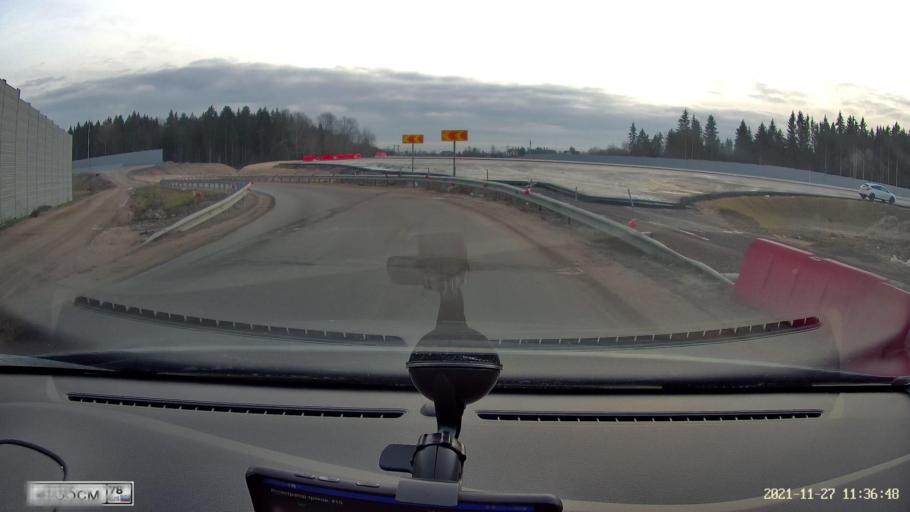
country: RU
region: Leningrad
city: Russko-Vysotskoye
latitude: 59.6971
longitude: 29.9815
